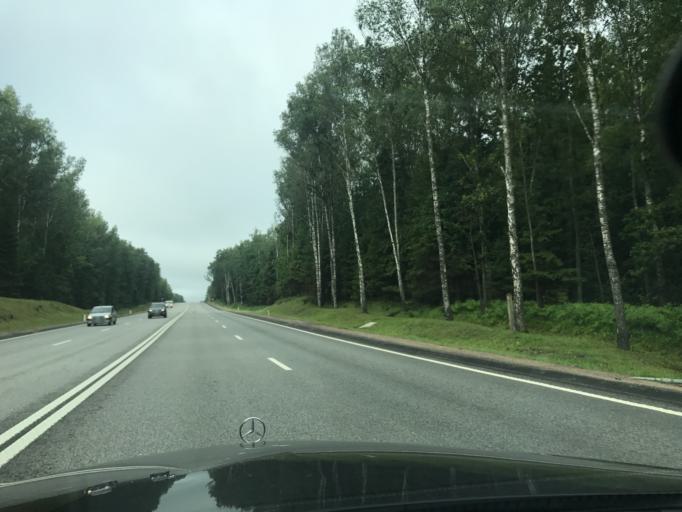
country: RU
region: Smolensk
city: Vyaz'ma
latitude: 55.3096
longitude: 34.5154
